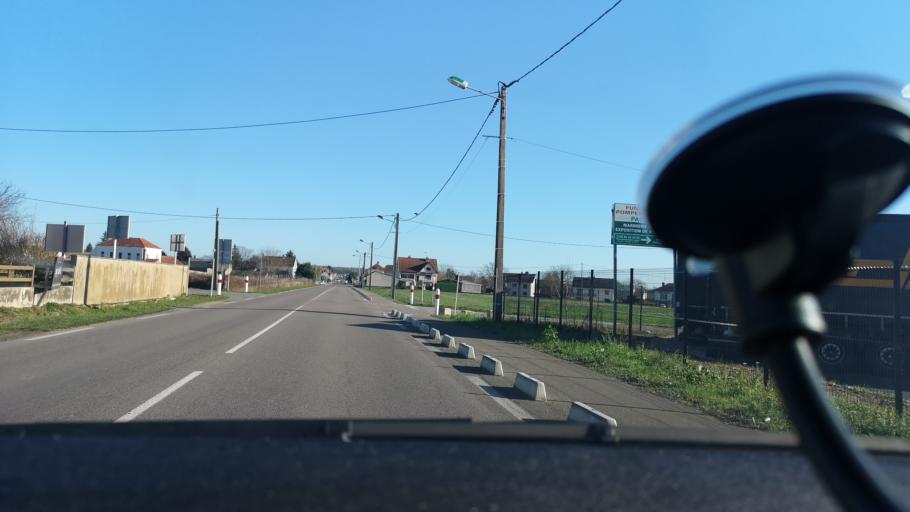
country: FR
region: Bourgogne
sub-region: Departement de Saone-et-Loire
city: Saint-Marcel
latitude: 46.7830
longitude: 4.9143
